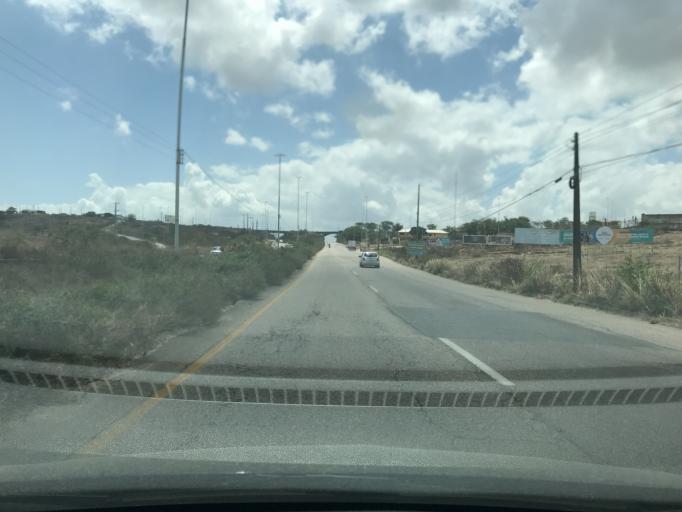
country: BR
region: Pernambuco
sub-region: Caruaru
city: Caruaru
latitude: -8.3071
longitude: -35.9601
